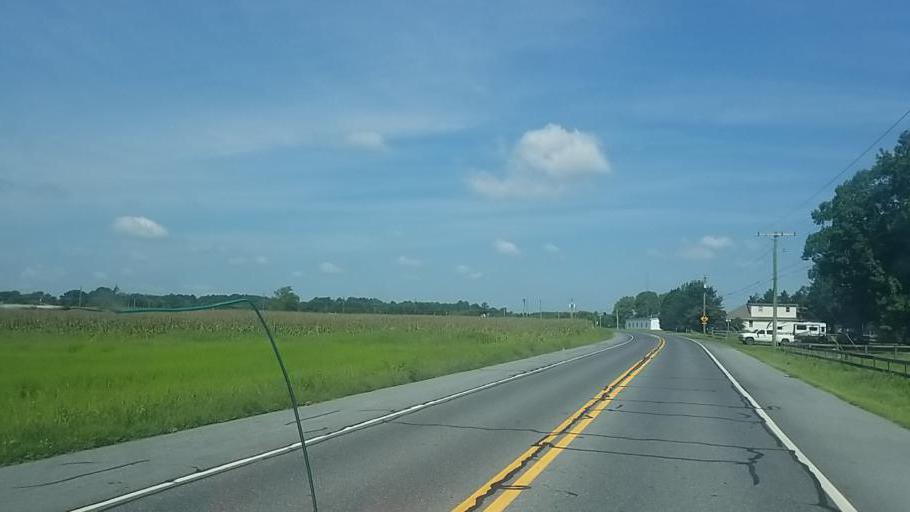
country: US
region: Delaware
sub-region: Sussex County
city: Seaford
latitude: 38.6830
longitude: -75.5868
